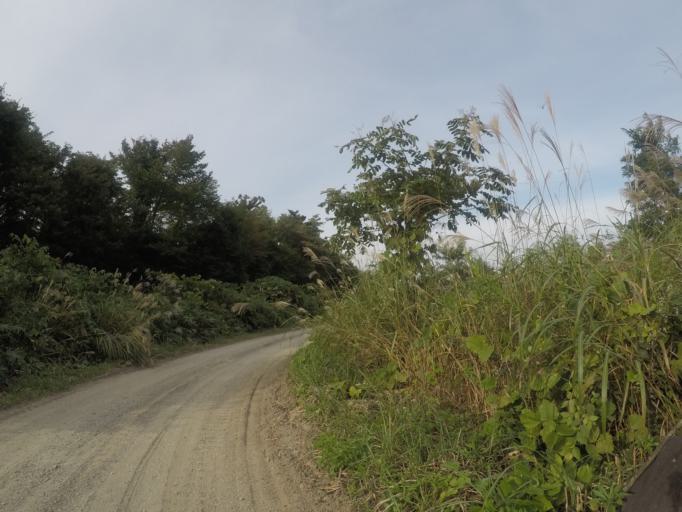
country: JP
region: Fukushima
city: Fukushima-shi
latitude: 37.7134
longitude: 140.3576
